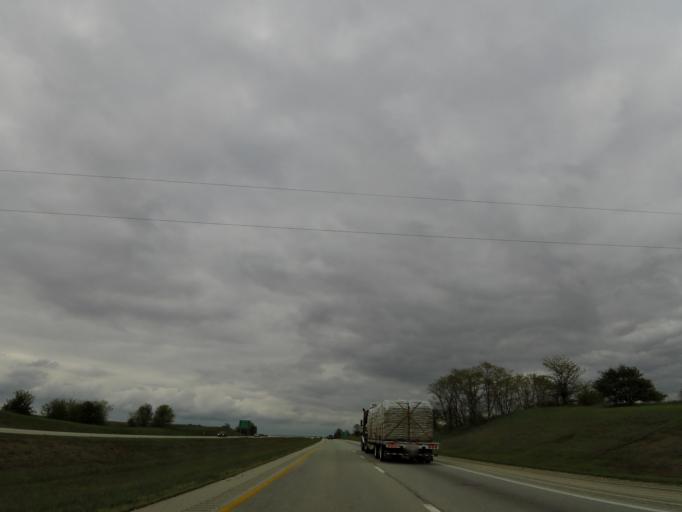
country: US
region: Ohio
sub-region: Greene County
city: Jamestown
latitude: 39.5533
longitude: -83.7287
